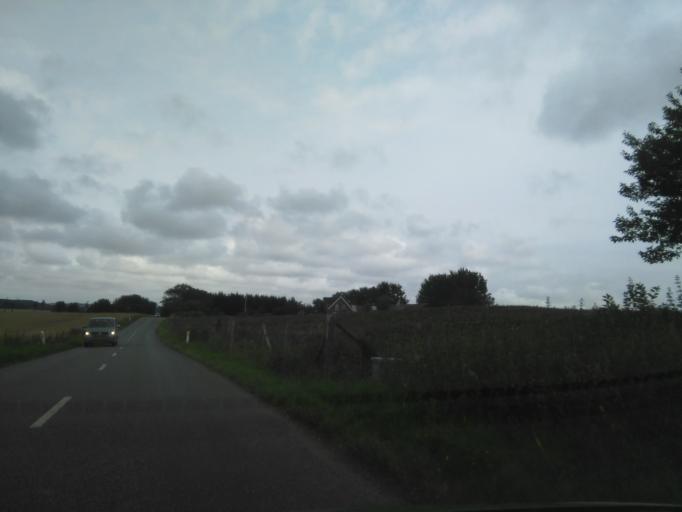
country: DK
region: Central Jutland
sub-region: Odder Kommune
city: Odder
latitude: 55.9515
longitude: 10.1098
